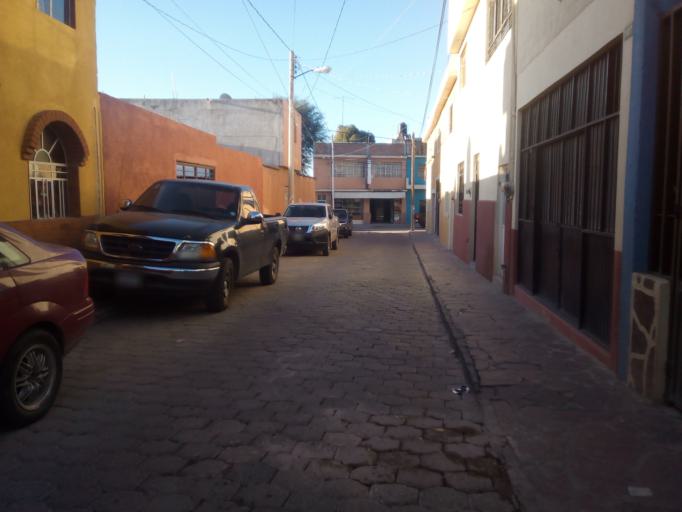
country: MX
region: Guerrero
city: San Luis de la Paz
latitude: 21.2942
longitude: -100.5154
